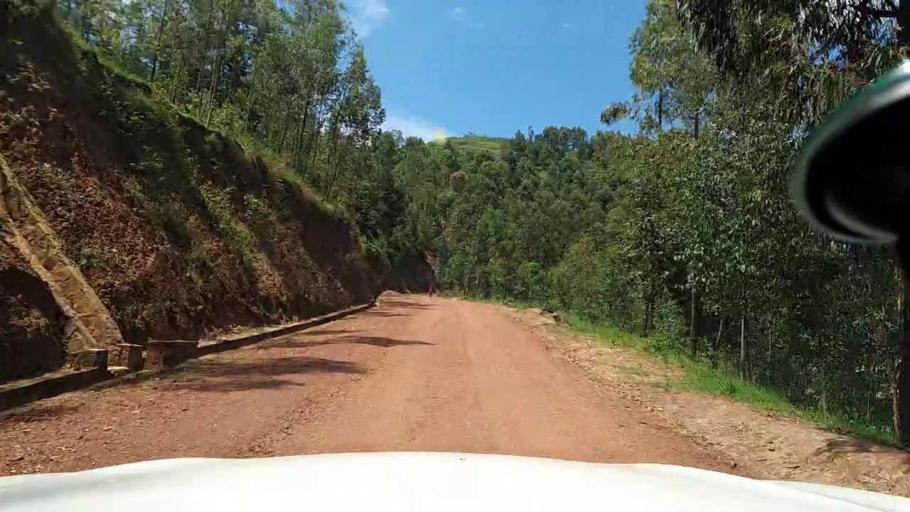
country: RW
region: Northern Province
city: Byumba
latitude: -1.7375
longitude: 29.8595
